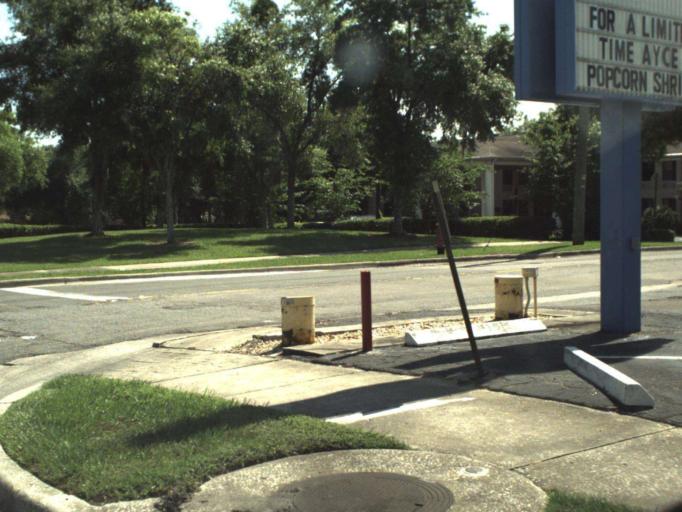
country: US
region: Florida
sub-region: Marion County
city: Ocala
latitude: 29.1770
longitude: -82.1406
